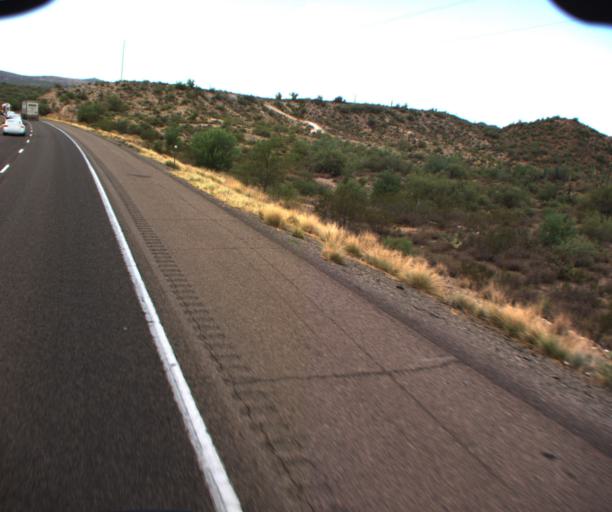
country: US
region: Arizona
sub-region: Yavapai County
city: Black Canyon City
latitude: 34.0219
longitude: -112.1485
